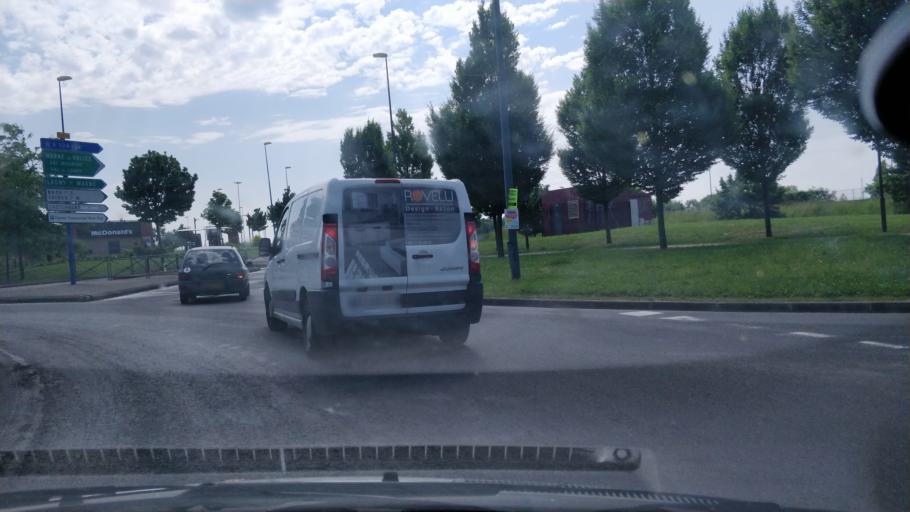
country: FR
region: Ile-de-France
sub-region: Departement de Seine-et-Marne
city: Chelles
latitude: 48.8766
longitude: 2.6008
